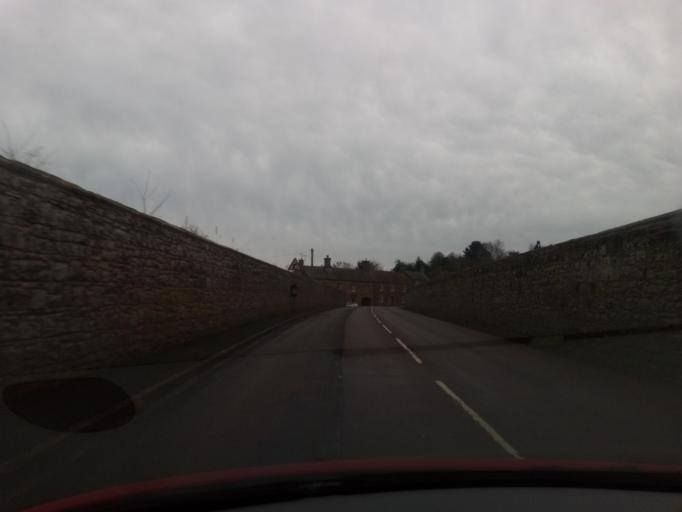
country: GB
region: England
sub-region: Northumberland
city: Alnwick
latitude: 55.4191
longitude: -1.7144
